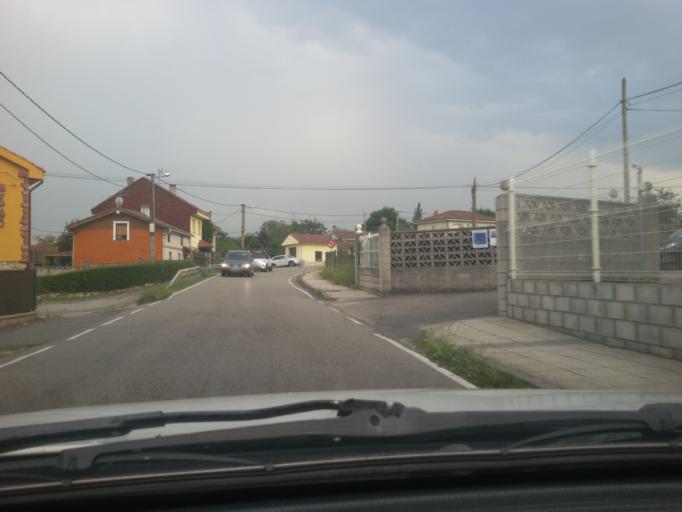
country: ES
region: Asturias
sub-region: Province of Asturias
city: Lugones
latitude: 43.4060
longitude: -5.7944
